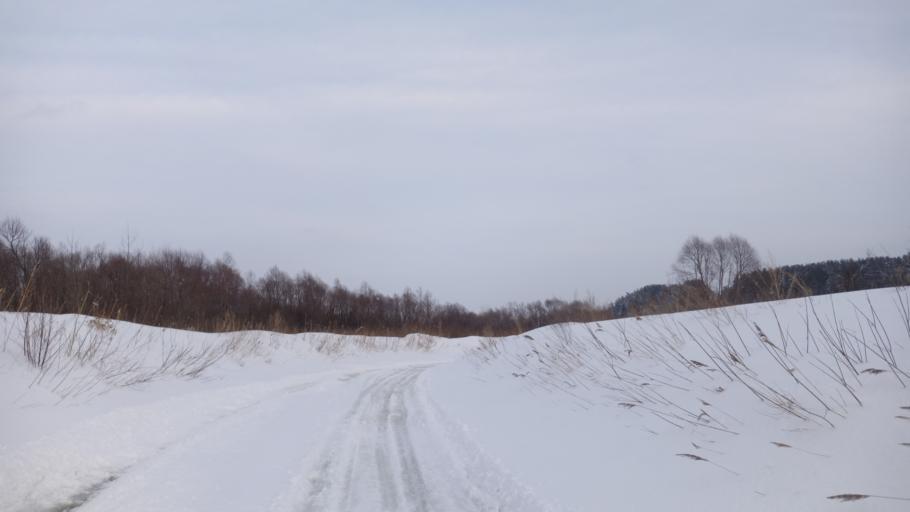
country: RU
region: Altai Krai
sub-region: Gorod Barnaulskiy
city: Barnaul
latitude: 53.3097
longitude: 83.7273
